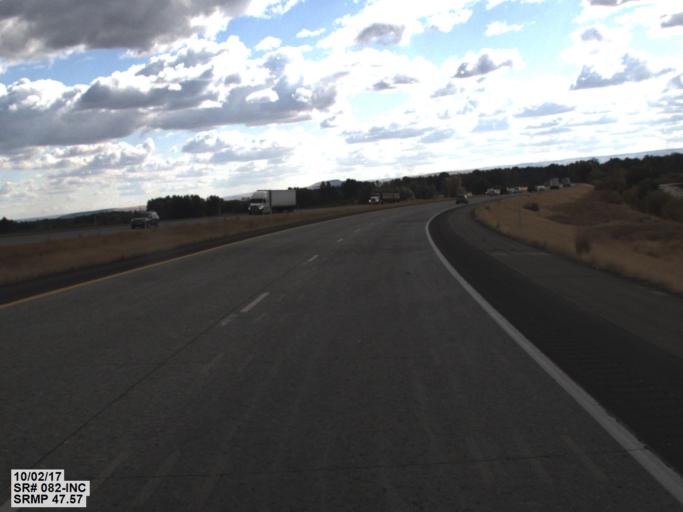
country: US
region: Washington
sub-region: Yakima County
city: Toppenish
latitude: 46.4407
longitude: -120.3456
